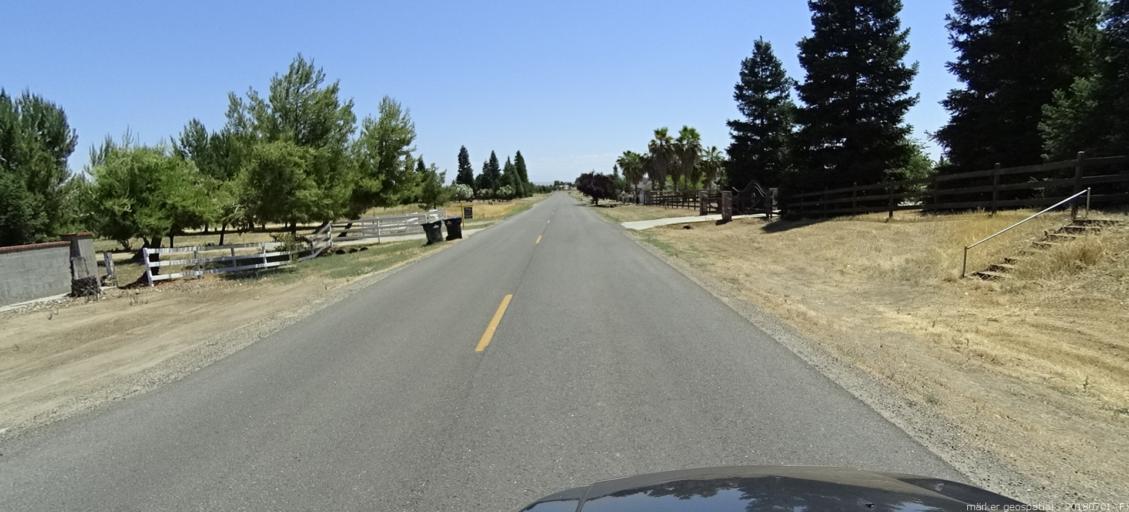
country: US
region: California
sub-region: Madera County
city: Madera Acres
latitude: 37.0675
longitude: -120.0137
